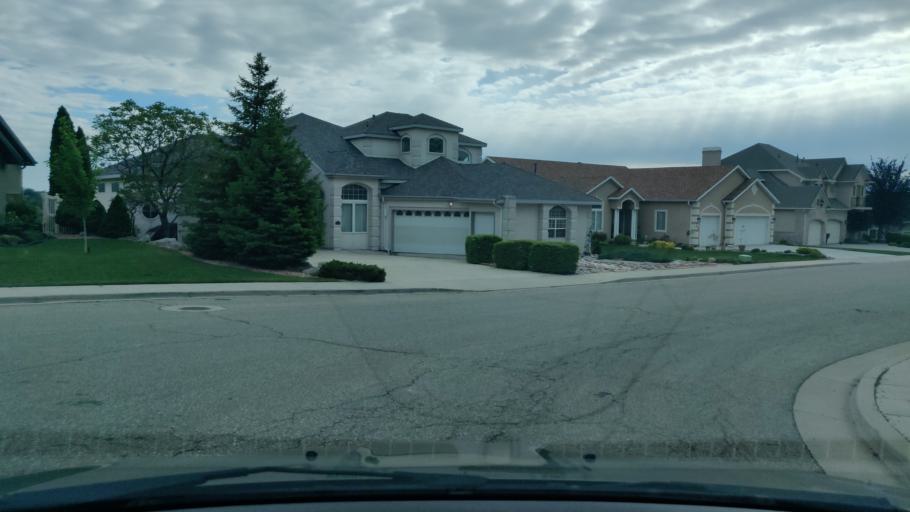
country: US
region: Utah
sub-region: Salt Lake County
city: Cottonwood Heights
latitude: 40.6069
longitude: -111.8139
